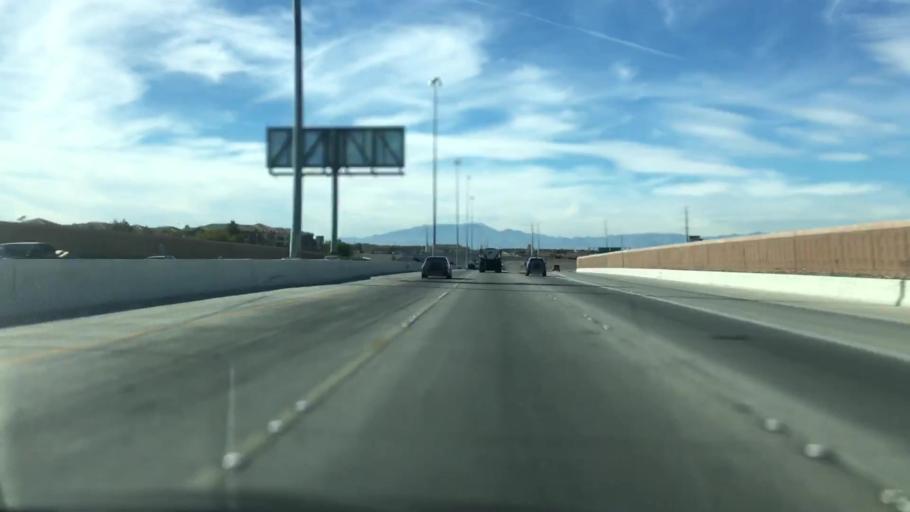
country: US
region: Nevada
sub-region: Clark County
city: Whitney
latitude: 36.0302
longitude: -115.0410
